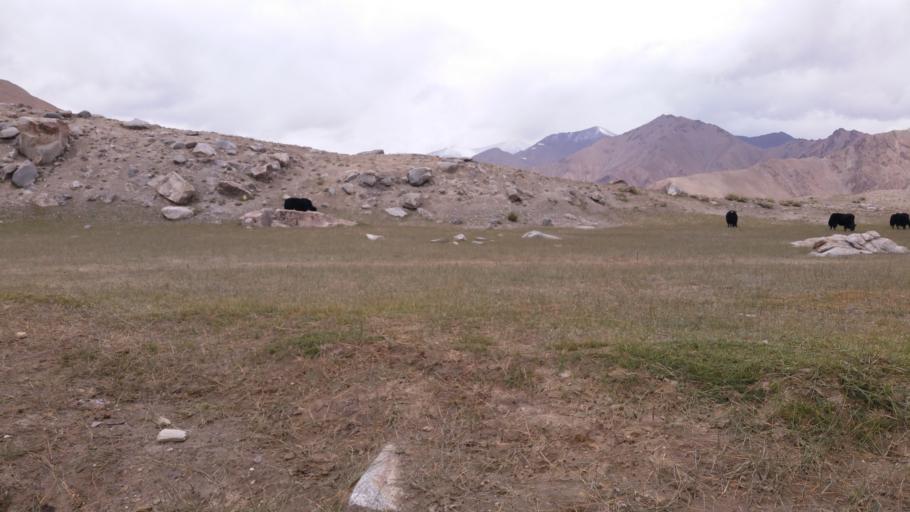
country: CN
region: Xinjiang Uygur Zizhiqu
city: Kekeya'er Ke'erkezizu
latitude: 38.4575
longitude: 75.0529
